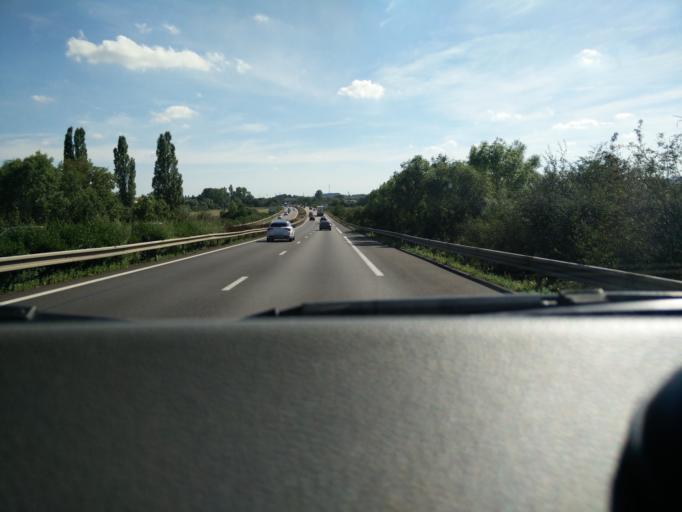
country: FR
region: Lorraine
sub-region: Departement de la Moselle
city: Bertrange
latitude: 49.3167
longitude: 6.1824
